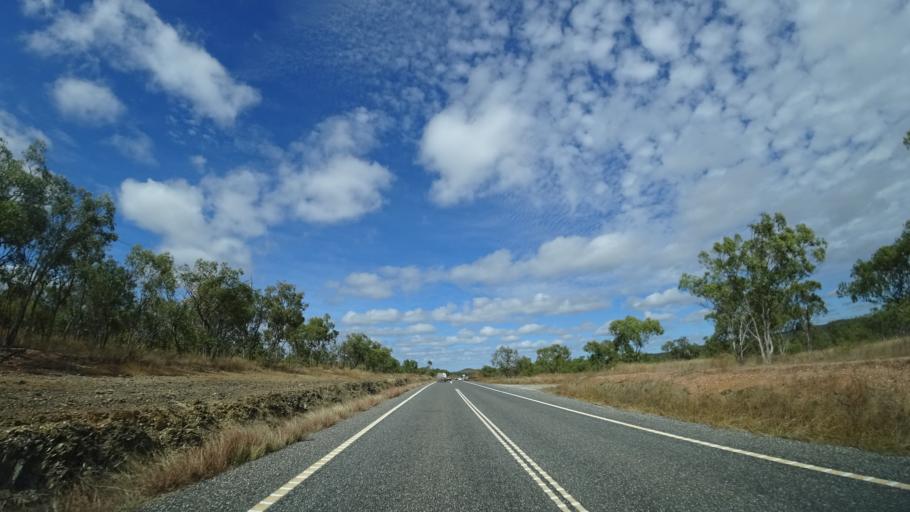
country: AU
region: Queensland
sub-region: Cairns
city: Port Douglas
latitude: -16.3786
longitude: 144.7360
